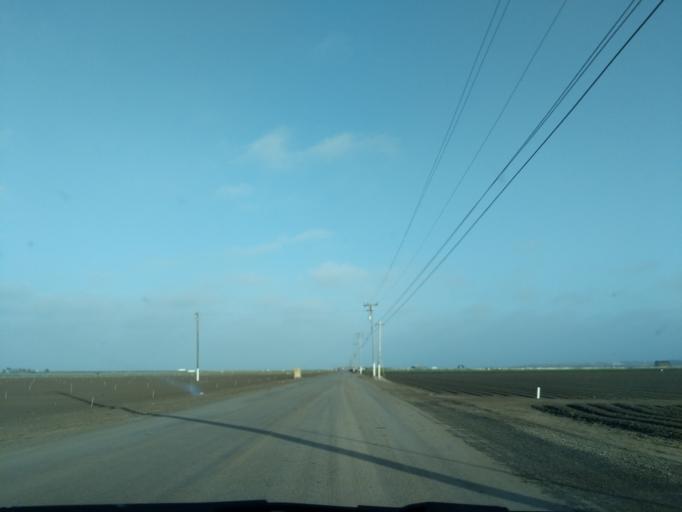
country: US
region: California
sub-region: Monterey County
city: Castroville
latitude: 36.7564
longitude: -121.7833
